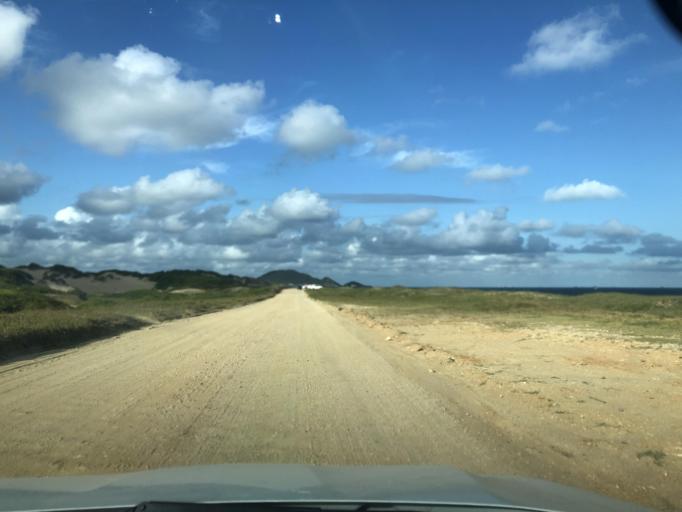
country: BR
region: Santa Catarina
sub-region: Sao Francisco Do Sul
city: Sao Francisco do Sul
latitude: -26.2548
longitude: -48.5156
